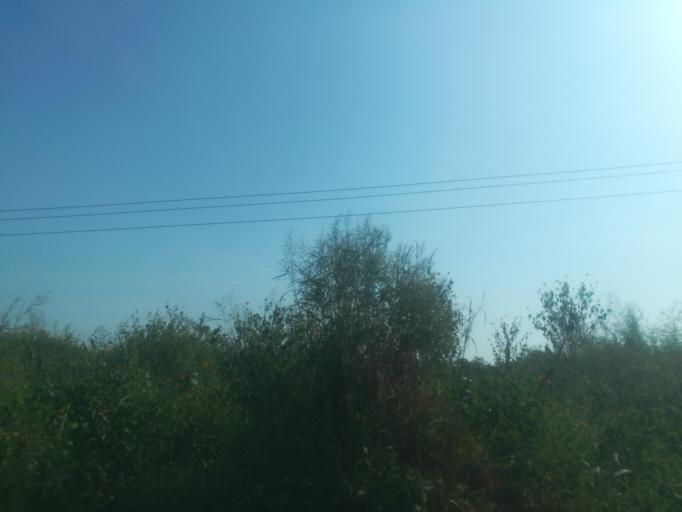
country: NG
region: Ogun
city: Abeokuta
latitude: 7.1373
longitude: 3.2865
